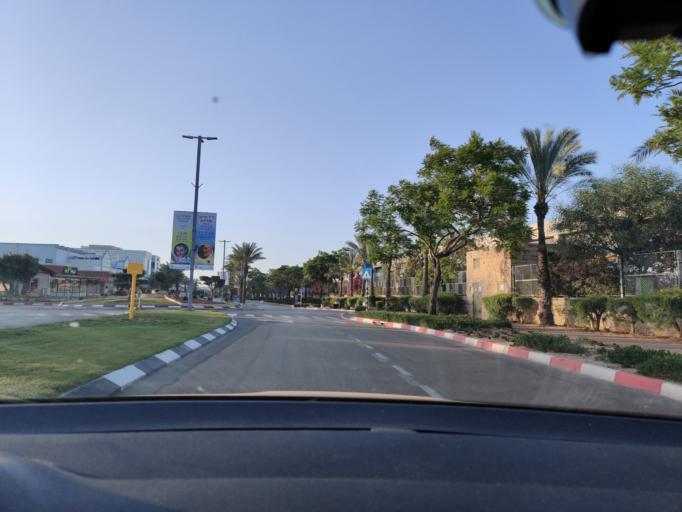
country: IL
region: Haifa
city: Qesarya
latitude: 32.4811
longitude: 34.9482
